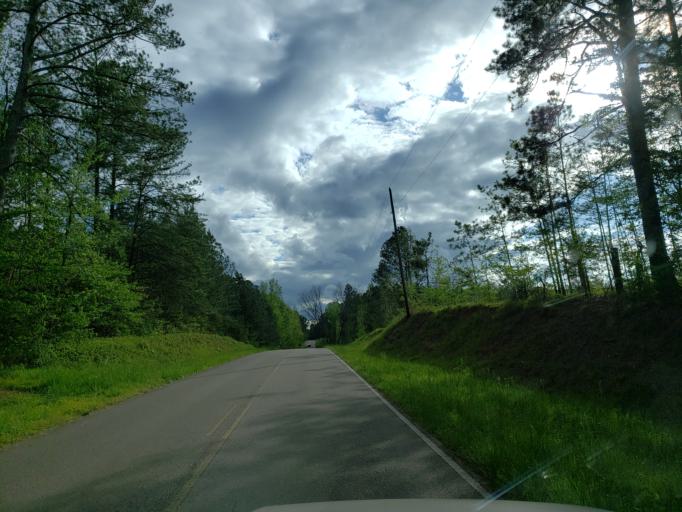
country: US
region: Georgia
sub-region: Haralson County
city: Tallapoosa
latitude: 33.8479
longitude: -85.3845
